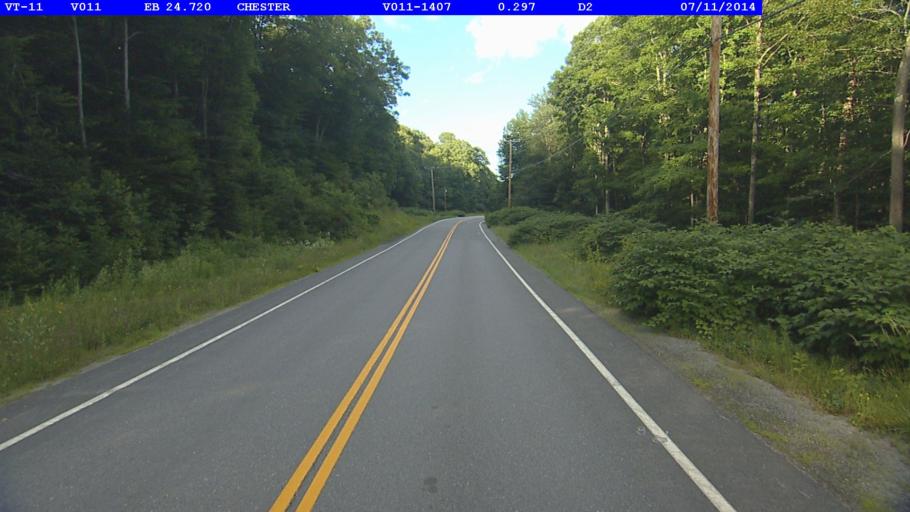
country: US
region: Vermont
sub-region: Windsor County
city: Chester
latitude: 43.2576
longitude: -72.6784
